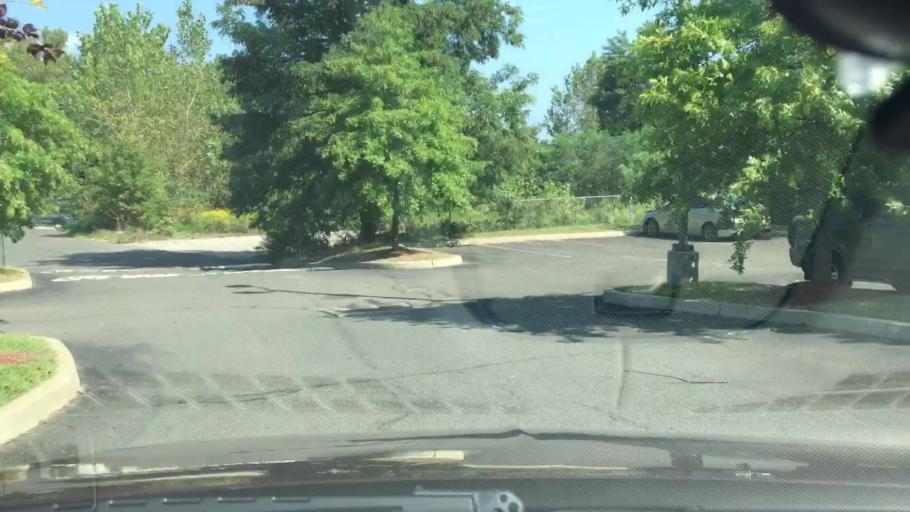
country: US
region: Connecticut
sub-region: Fairfield County
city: Danbury
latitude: 41.4199
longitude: -73.4184
